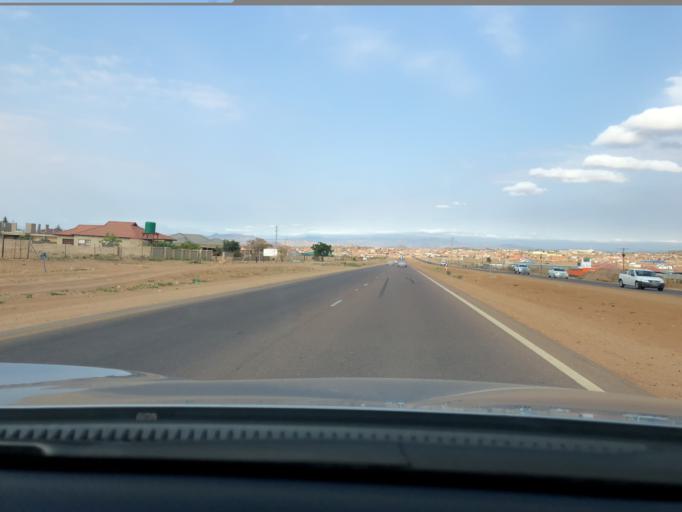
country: ZA
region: Limpopo
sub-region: Capricorn District Municipality
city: Mankoeng
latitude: -23.8879
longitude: 29.6771
